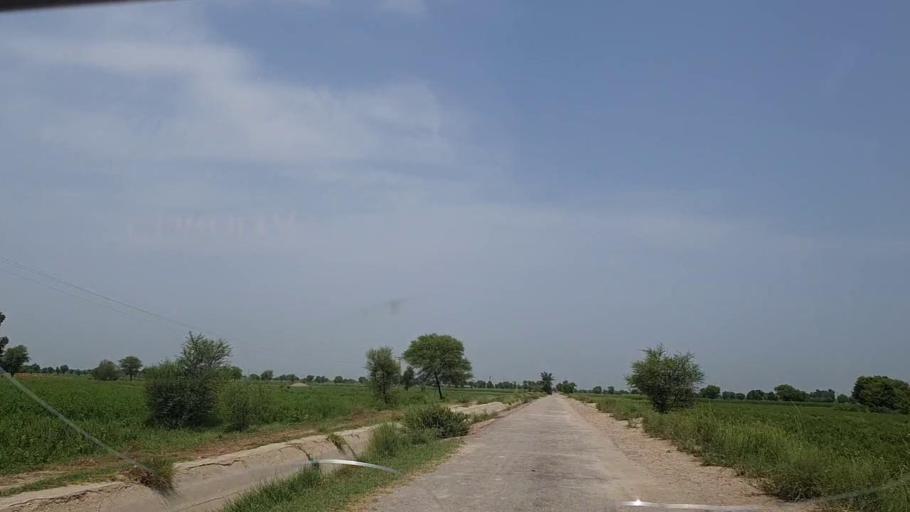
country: PK
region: Sindh
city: Tharu Shah
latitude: 26.9297
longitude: 68.0684
